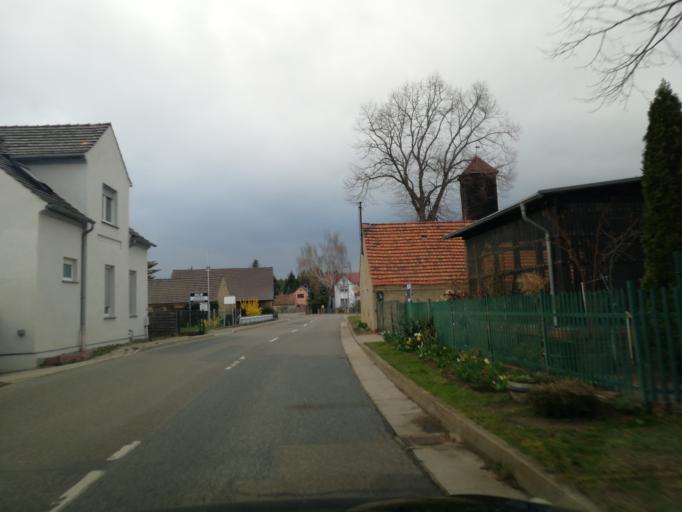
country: DE
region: Brandenburg
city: Vetschau
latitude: 51.7141
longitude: 14.0875
